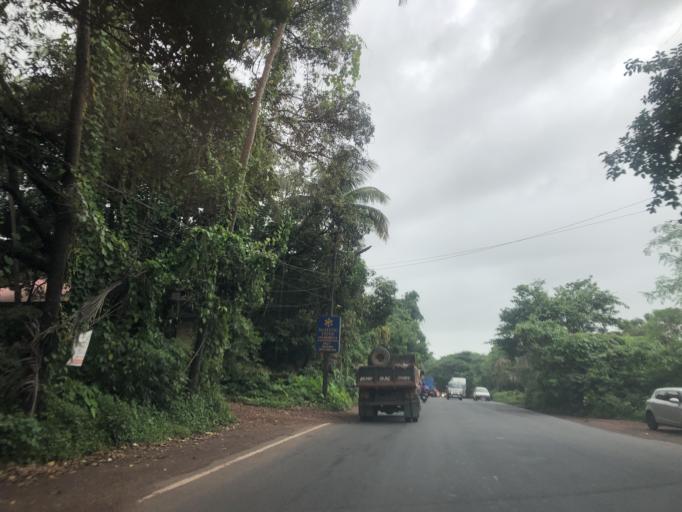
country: IN
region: Goa
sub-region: North Goa
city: Serula
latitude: 15.5456
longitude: 73.8197
